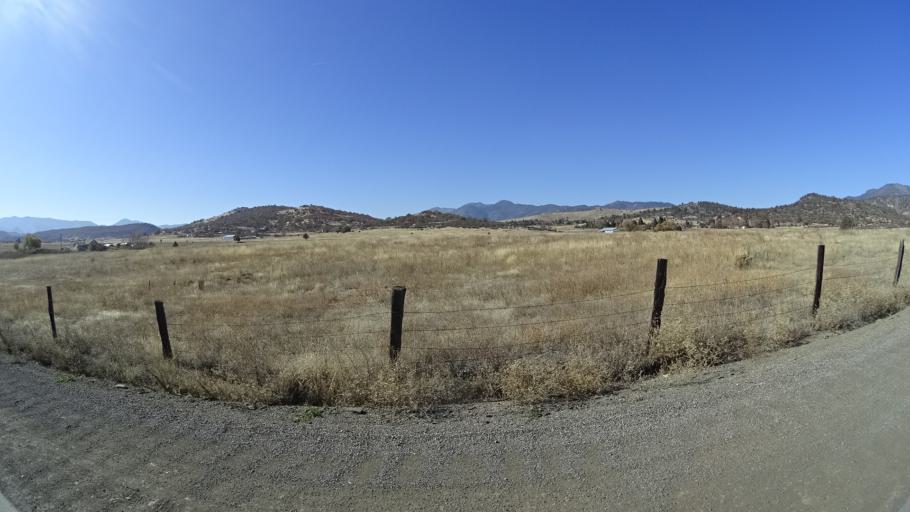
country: US
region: California
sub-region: Siskiyou County
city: Yreka
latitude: 41.7401
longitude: -122.5933
